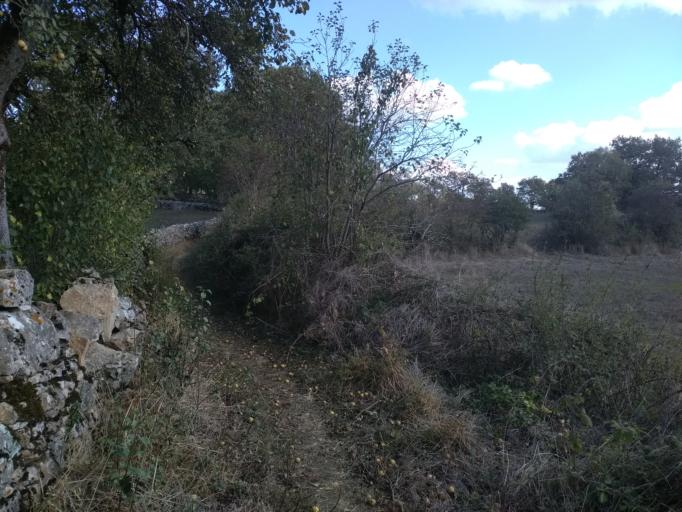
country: FR
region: Midi-Pyrenees
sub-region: Departement de l'Aveyron
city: Bozouls
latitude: 44.4775
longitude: 2.6939
